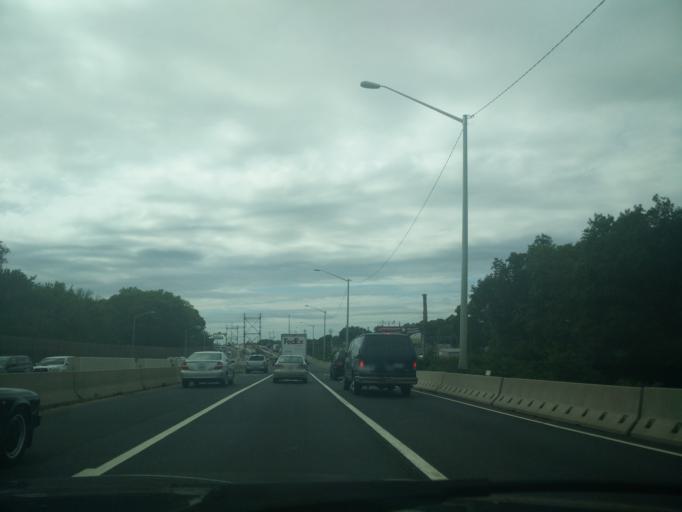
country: US
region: Connecticut
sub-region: New Haven County
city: City of Milford (balance)
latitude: 41.2077
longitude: -73.0977
